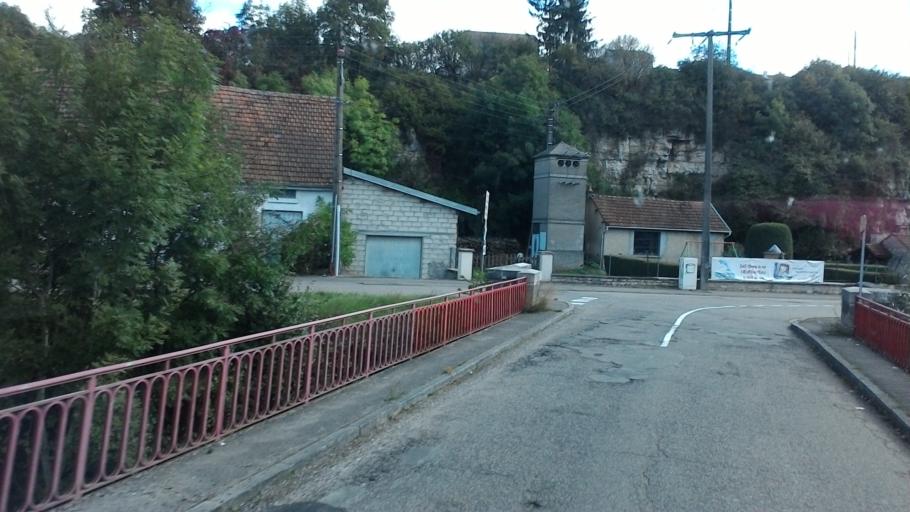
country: FR
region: Lorraine
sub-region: Departement des Vosges
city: Neufchateau
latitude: 48.3667
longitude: 5.6892
